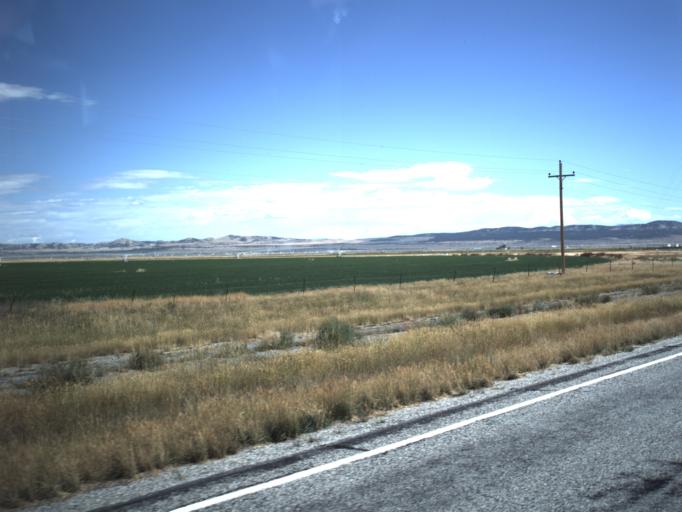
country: US
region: Idaho
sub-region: Oneida County
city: Malad City
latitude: 41.9663
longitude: -112.9362
